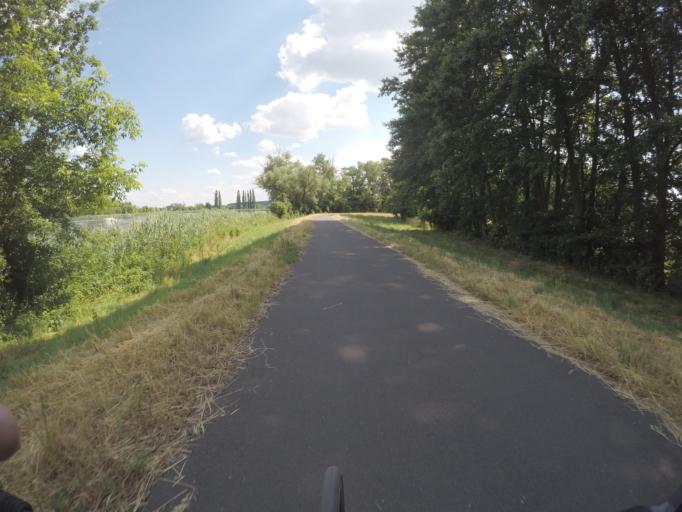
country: DE
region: Brandenburg
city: Ketzin
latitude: 52.4430
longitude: 12.8784
